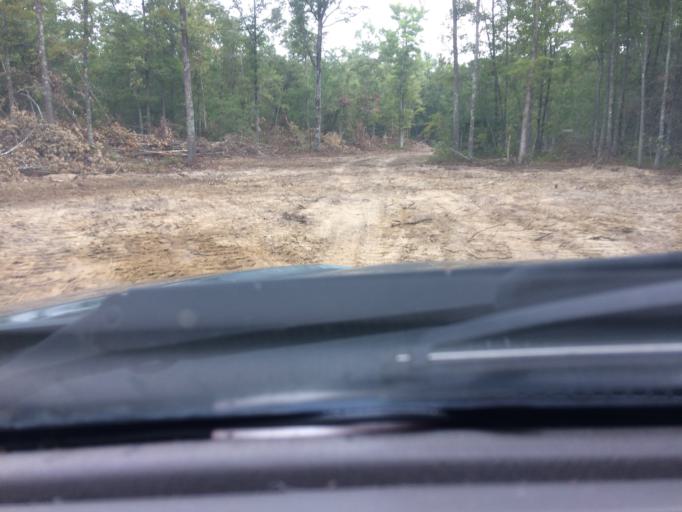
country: US
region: Tennessee
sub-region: Fentress County
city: Grimsley
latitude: 36.1875
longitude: -84.8959
